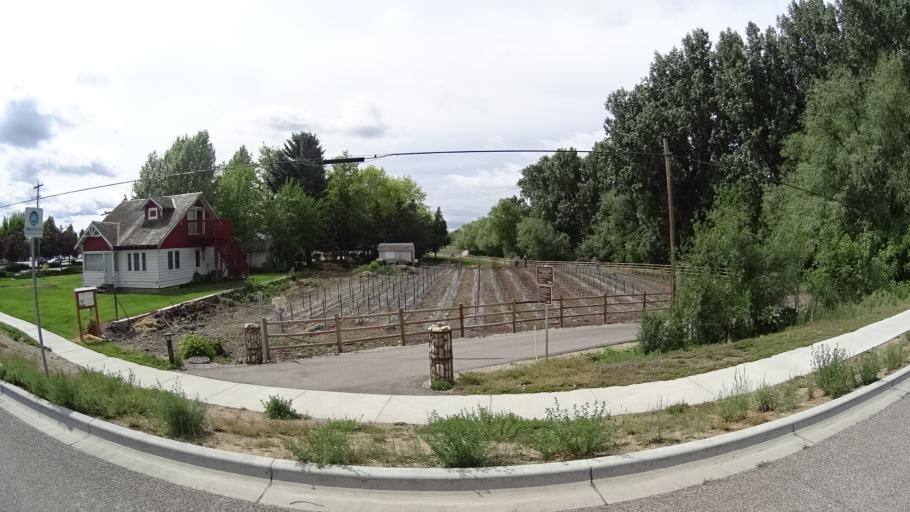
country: US
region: Idaho
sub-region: Ada County
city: Eagle
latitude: 43.6956
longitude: -116.3687
